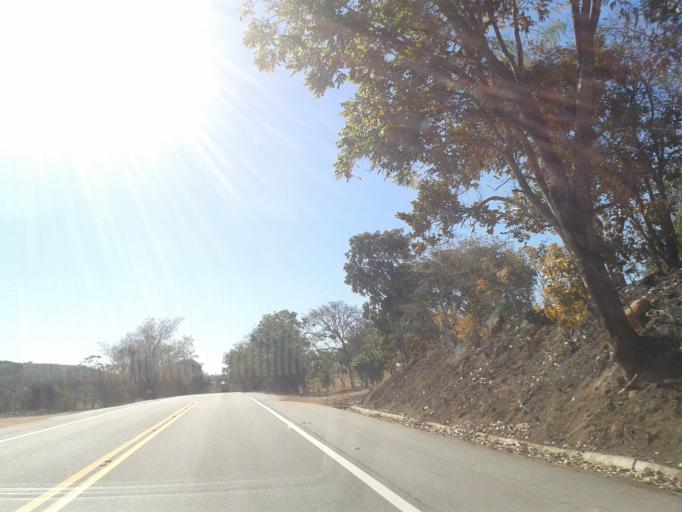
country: BR
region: Goias
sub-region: Itapuranga
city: Itapuranga
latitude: -15.6063
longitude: -50.2508
